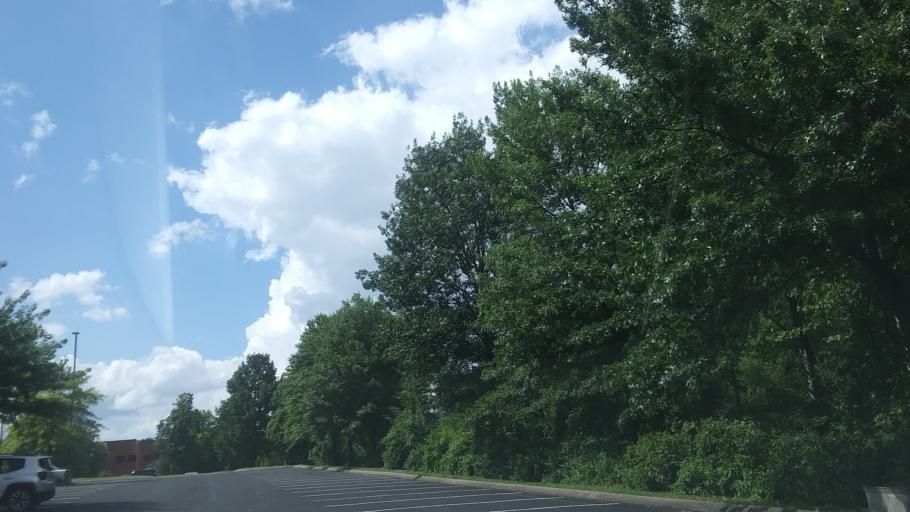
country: US
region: Tennessee
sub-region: Davidson County
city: Oak Hill
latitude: 36.0921
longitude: -86.7008
